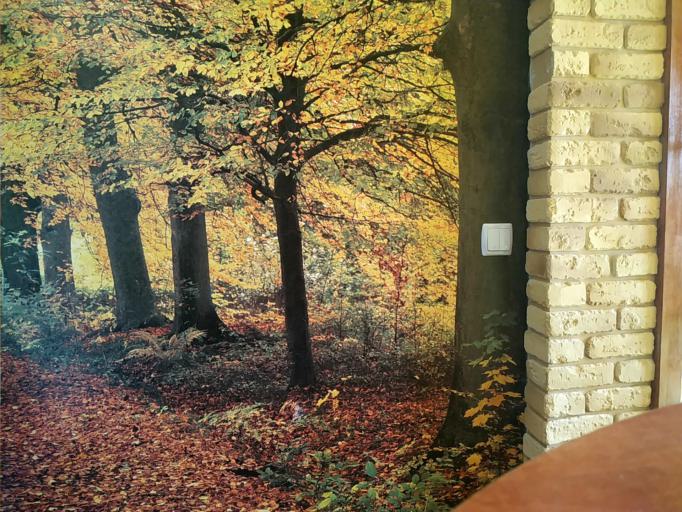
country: RU
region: Jaroslavl
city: Kukoboy
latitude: 58.8991
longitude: 39.6950
